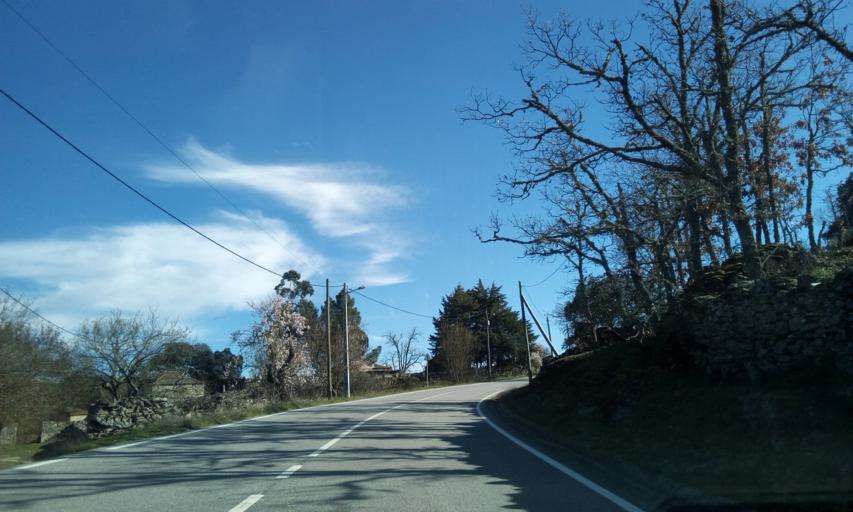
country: ES
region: Castille and Leon
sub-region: Provincia de Salamanca
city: Fuentes de Onoro
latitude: 40.6179
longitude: -6.8924
